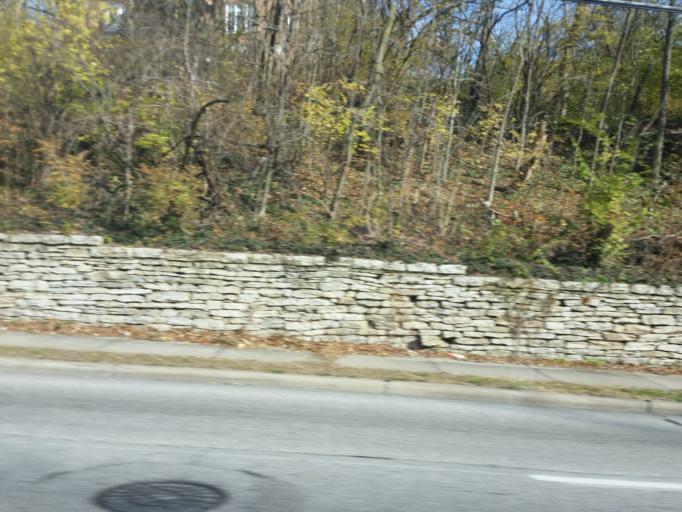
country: US
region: Ohio
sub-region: Hamilton County
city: Monfort Heights
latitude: 39.1737
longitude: -84.5620
